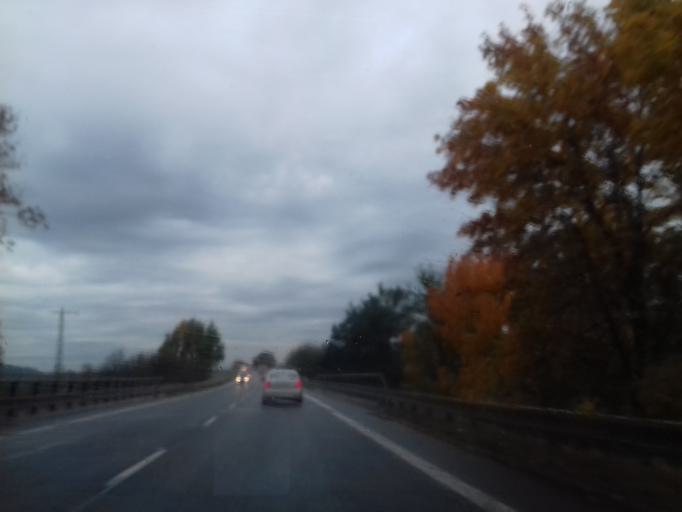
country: CZ
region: Pardubicky
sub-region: Okres Pardubice
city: Vysoke Myto
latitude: 49.9687
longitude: 16.1354
